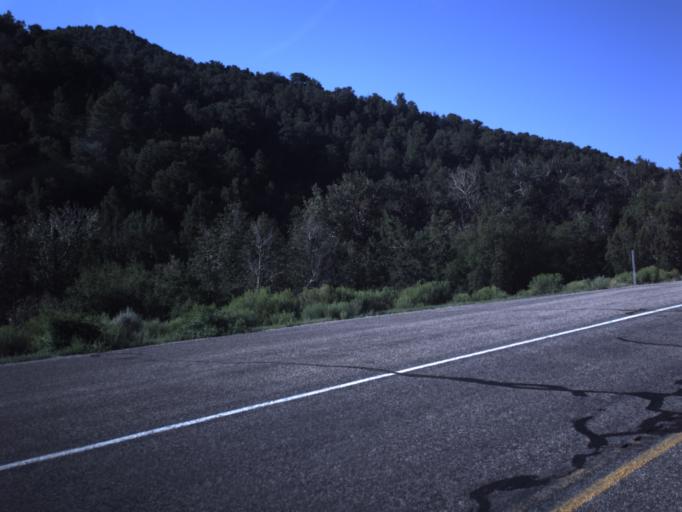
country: US
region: Utah
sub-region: Wayne County
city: Loa
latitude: 38.6654
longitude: -111.4264
